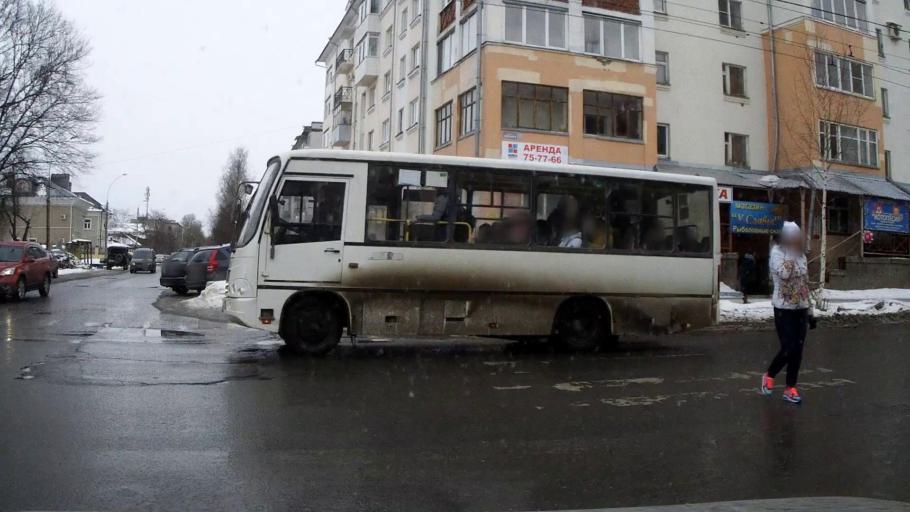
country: RU
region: Vologda
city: Vologda
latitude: 59.2275
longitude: 39.8997
